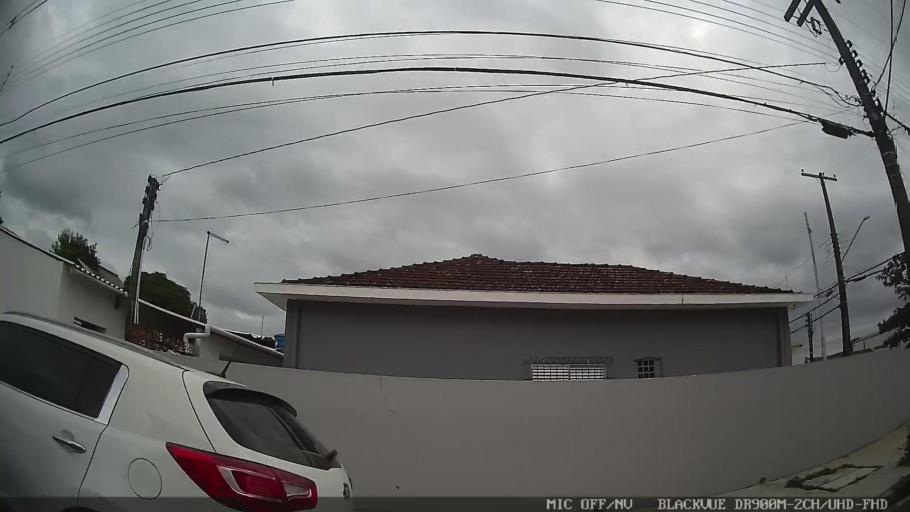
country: BR
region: Sao Paulo
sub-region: Guaruja
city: Guaruja
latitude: -23.9957
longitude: -46.2900
